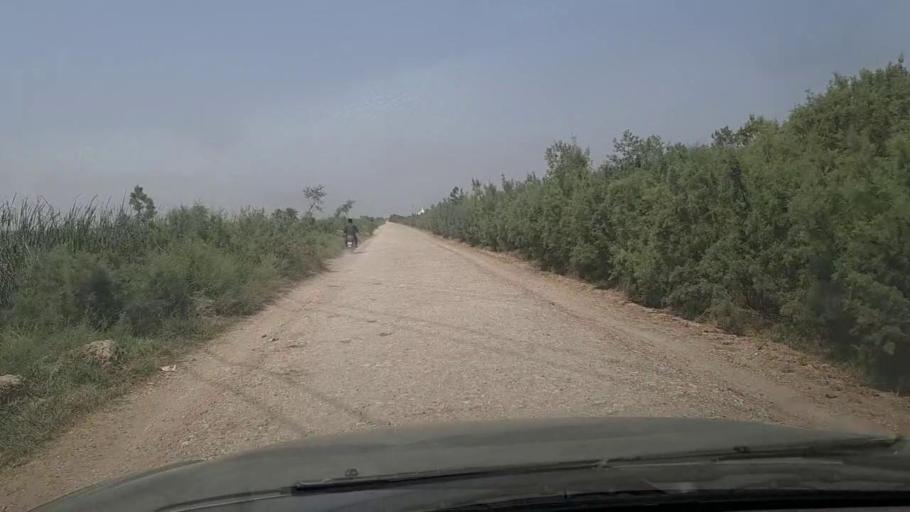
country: PK
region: Sindh
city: Adilpur
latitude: 27.9375
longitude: 69.2918
